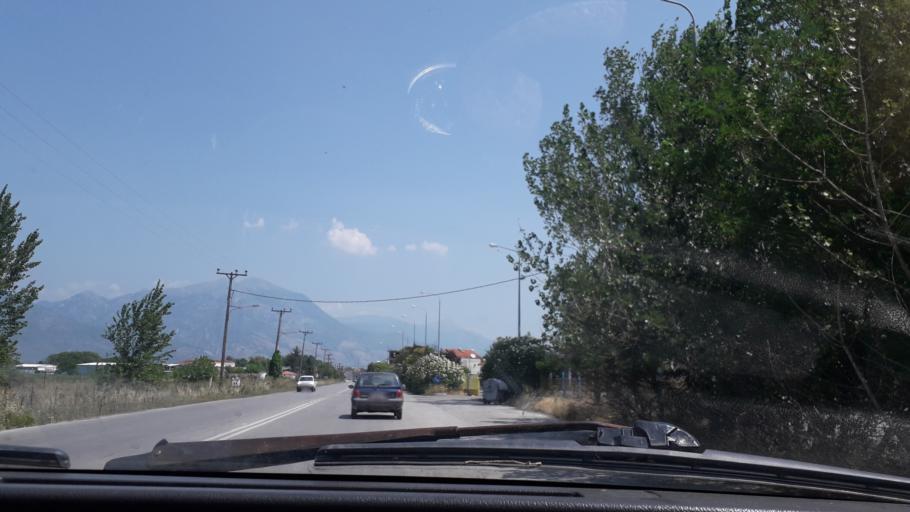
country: GR
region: Central Macedonia
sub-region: Nomos Pellis
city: Aridaia
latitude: 40.9645
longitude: 22.0521
